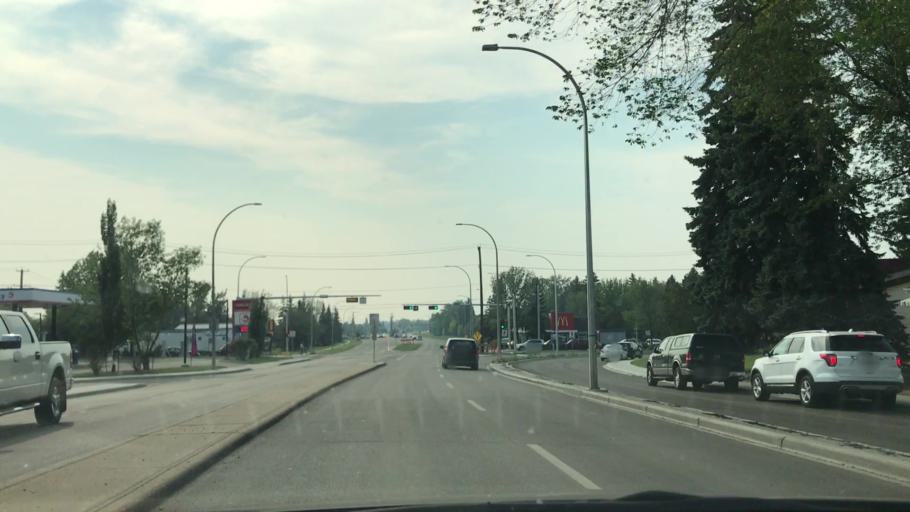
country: CA
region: Alberta
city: Edmonton
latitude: 53.4982
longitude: -113.5104
